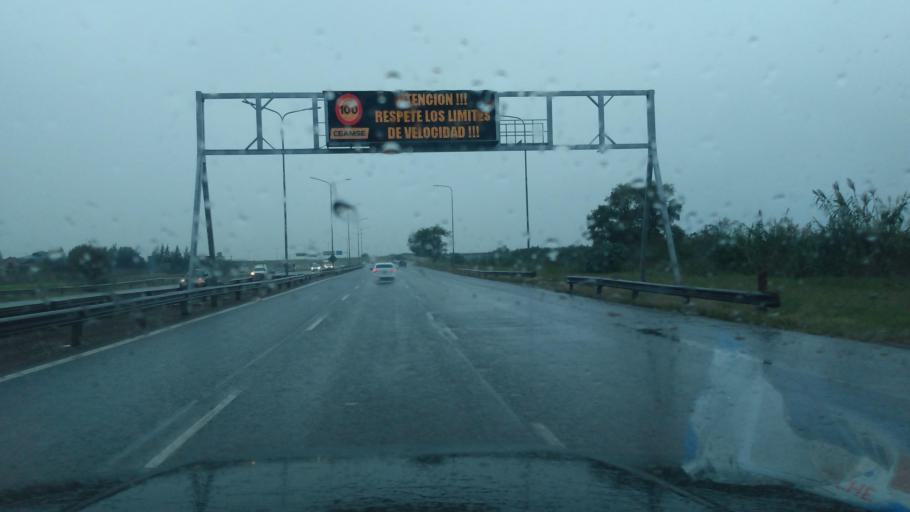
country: AR
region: Buenos Aires
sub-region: Partido de Tigre
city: Tigre
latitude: -34.4918
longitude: -58.5959
